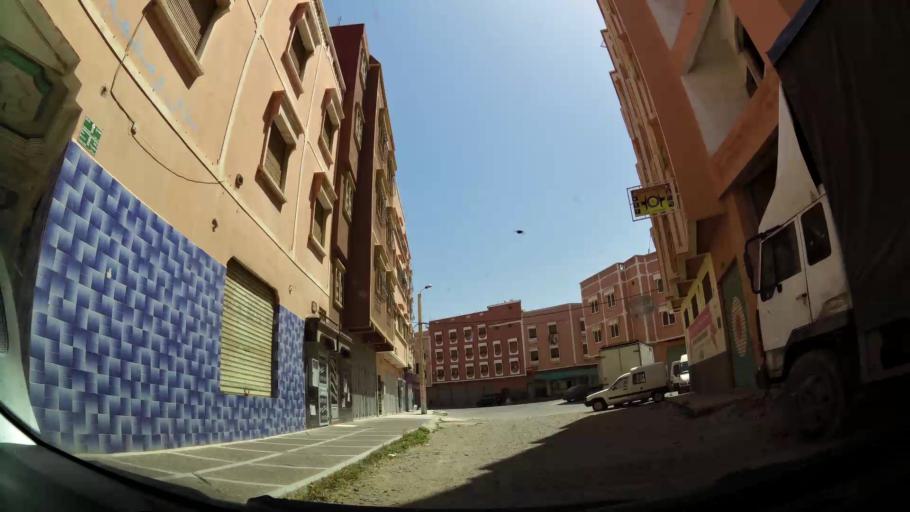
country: MA
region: Souss-Massa-Draa
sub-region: Inezgane-Ait Mellou
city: Inezgane
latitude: 30.3393
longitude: -9.5032
